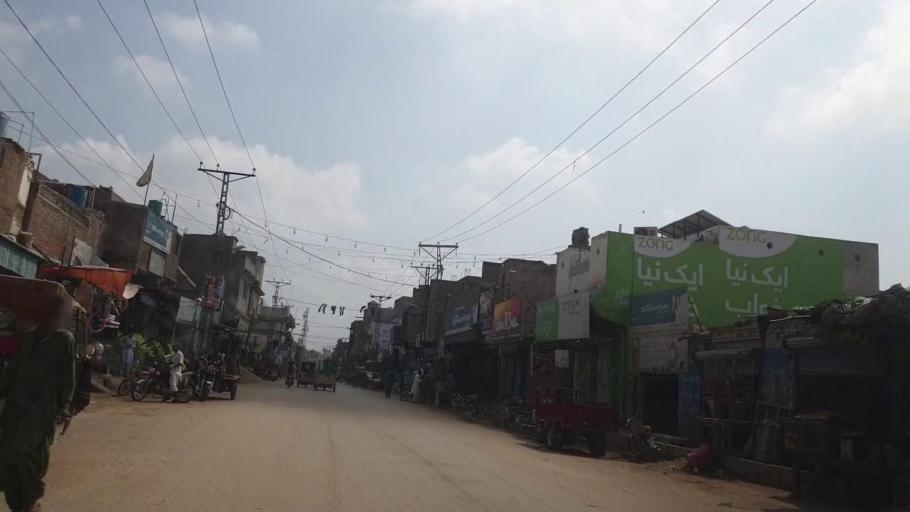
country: PK
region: Sindh
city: Khairpur
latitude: 27.5236
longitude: 68.7519
